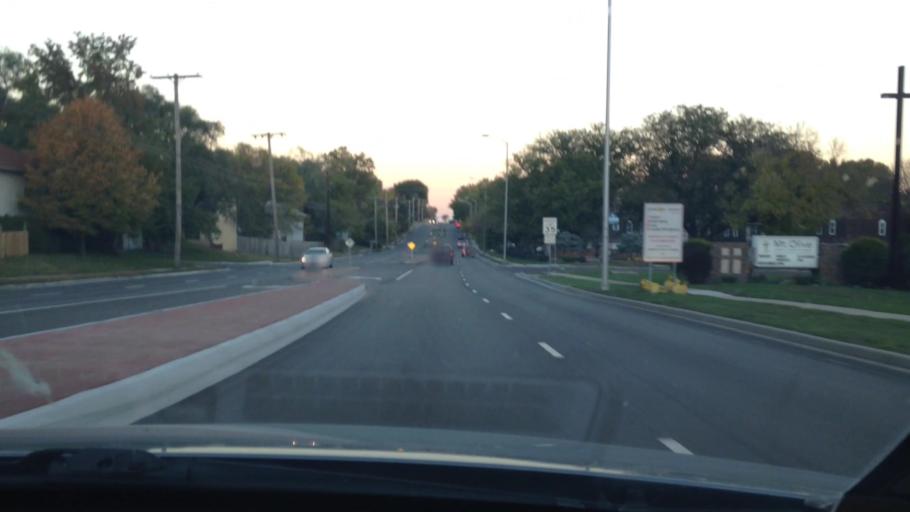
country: US
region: Kansas
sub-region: Johnson County
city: Lenexa
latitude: 38.9566
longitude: -94.7048
